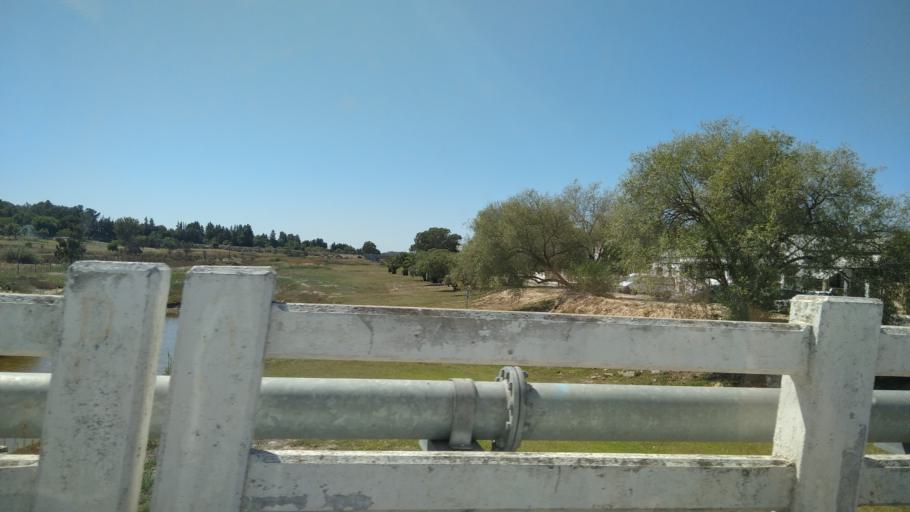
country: ZA
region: Western Cape
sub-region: West Coast District Municipality
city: Moorreesburg
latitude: -33.0622
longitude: 18.3455
